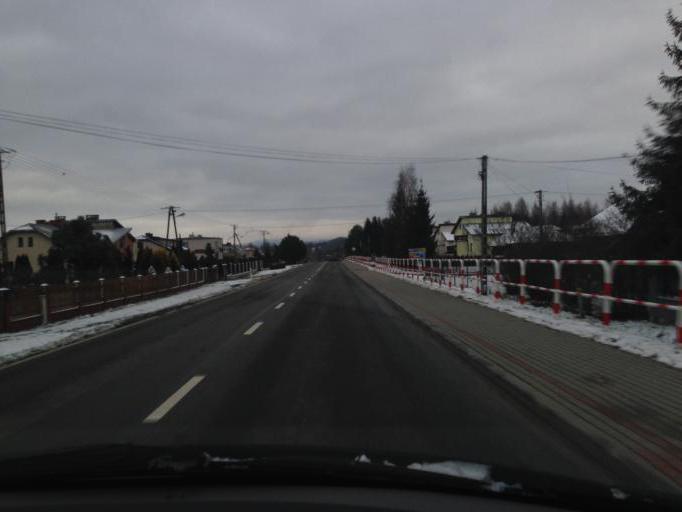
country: PL
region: Lesser Poland Voivodeship
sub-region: Powiat gorlicki
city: Gorlice
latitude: 49.7036
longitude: 21.1389
